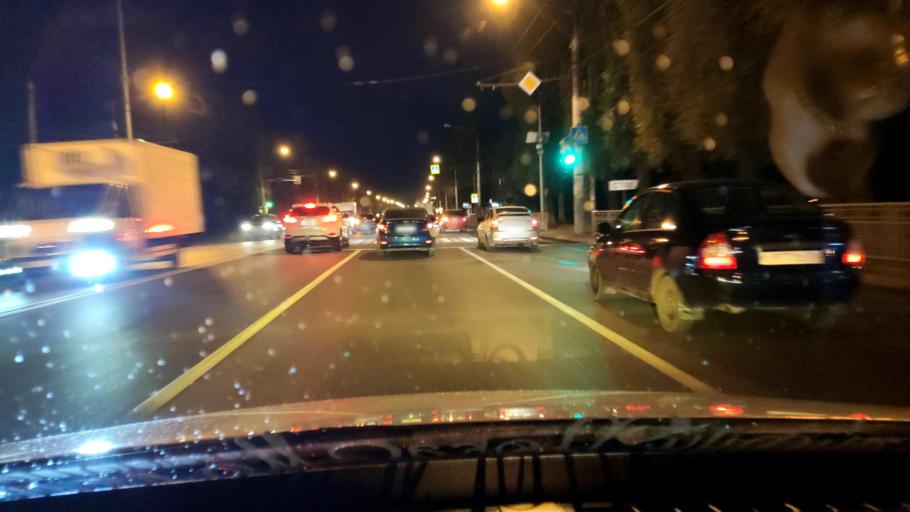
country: RU
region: Voronezj
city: Maslovka
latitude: 51.6104
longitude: 39.2372
